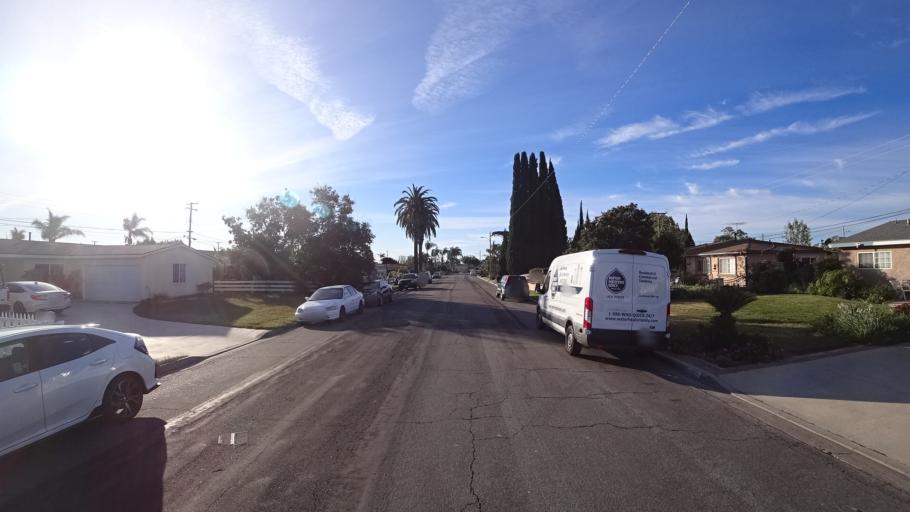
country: US
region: California
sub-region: Orange County
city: Garden Grove
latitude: 33.7693
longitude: -117.9494
